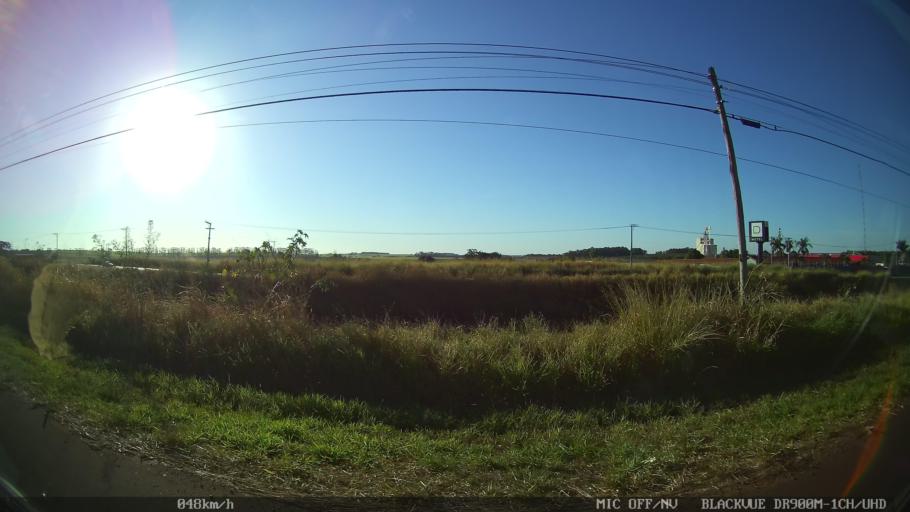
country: BR
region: Sao Paulo
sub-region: Guapiacu
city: Guapiacu
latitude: -20.7820
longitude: -49.2608
